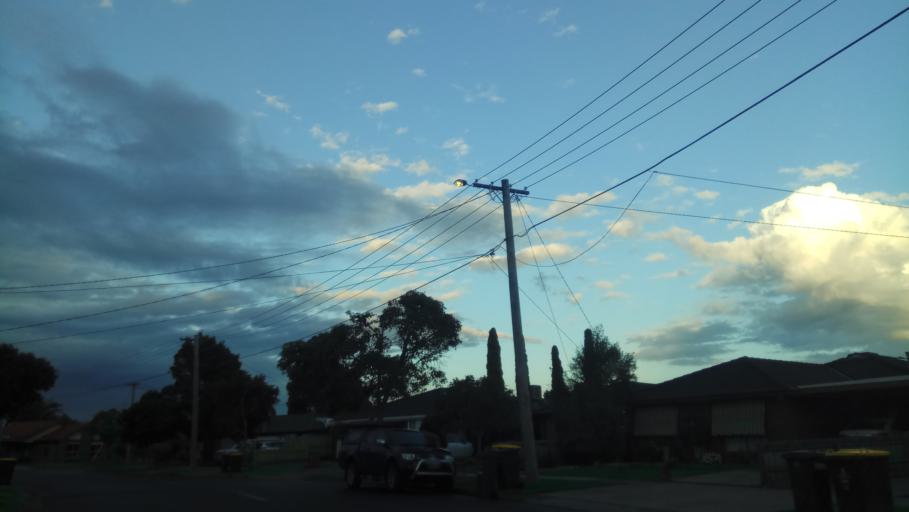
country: AU
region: Victoria
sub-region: Hobsons Bay
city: Altona Meadows
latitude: -37.8807
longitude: 144.7739
